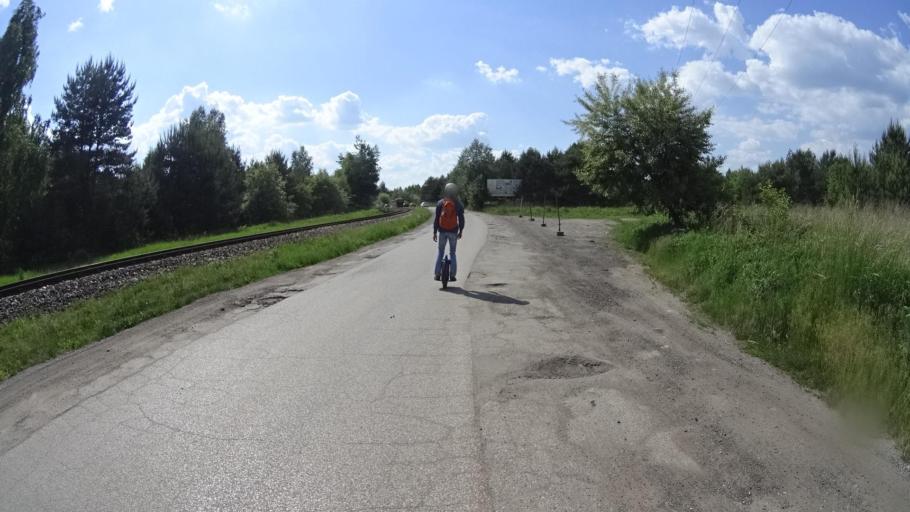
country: PL
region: Masovian Voivodeship
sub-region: Powiat piaseczynski
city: Jozefoslaw
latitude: 52.0964
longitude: 21.0783
